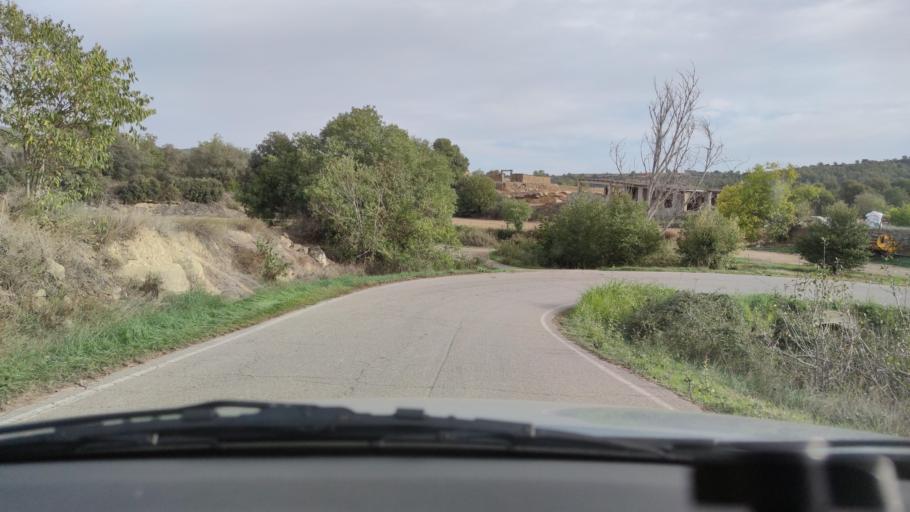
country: ES
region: Catalonia
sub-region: Provincia de Lleida
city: Artesa de Segre
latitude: 41.9080
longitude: 1.0408
